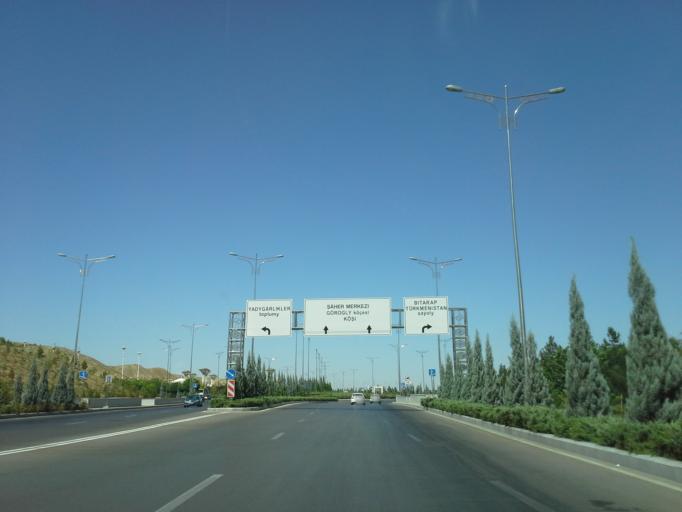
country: TM
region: Ahal
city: Ashgabat
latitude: 37.9305
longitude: 58.3174
